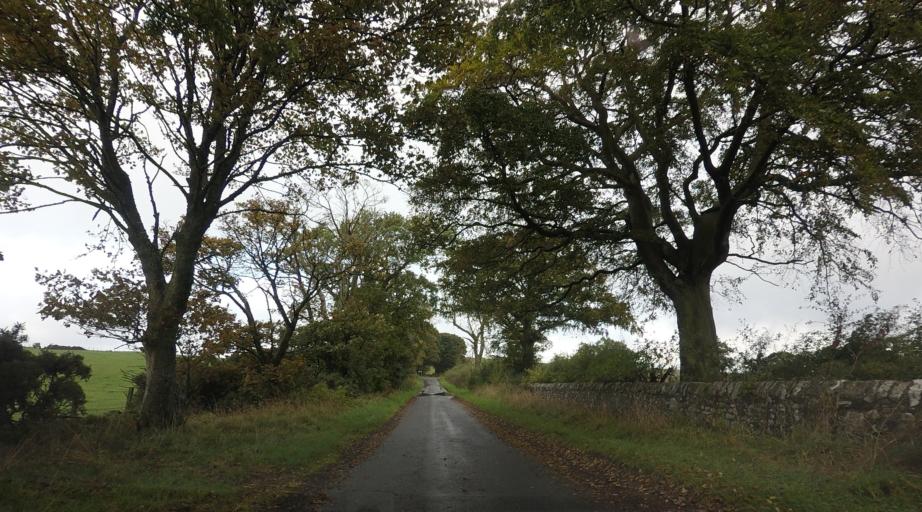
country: GB
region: Scotland
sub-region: Fife
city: Balmullo
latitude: 56.3635
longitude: -2.9743
